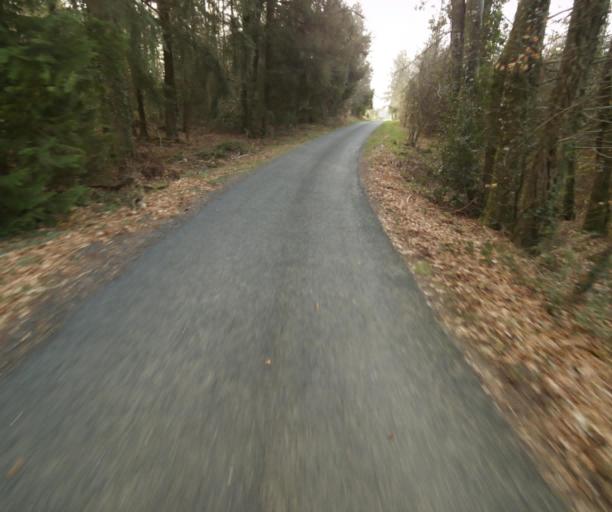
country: FR
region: Limousin
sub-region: Departement de la Correze
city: Chamboulive
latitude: 45.4366
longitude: 1.7602
